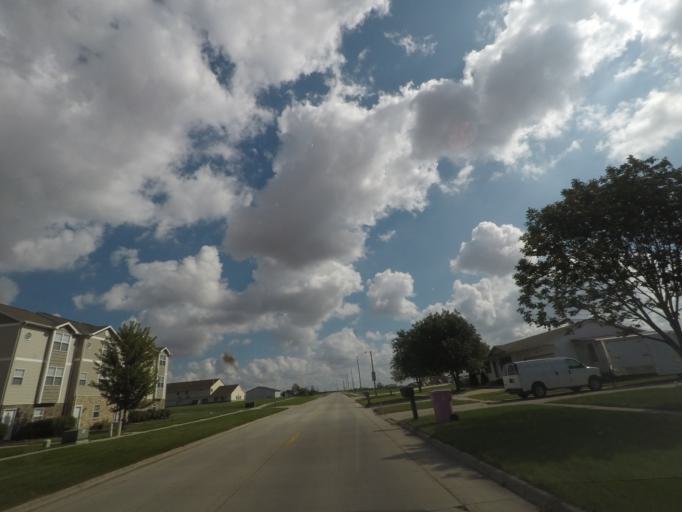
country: US
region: Iowa
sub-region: Story County
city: Nevada
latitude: 42.0052
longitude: -93.4405
